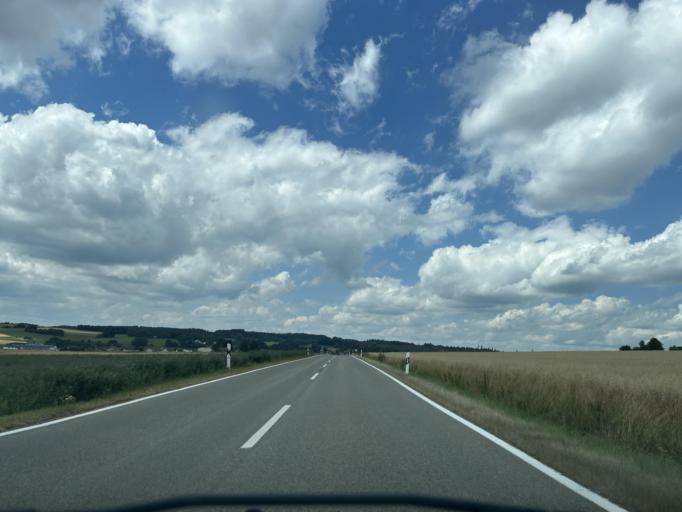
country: DE
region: Baden-Wuerttemberg
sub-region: Tuebingen Region
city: Leibertingen
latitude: 48.0425
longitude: 9.0272
